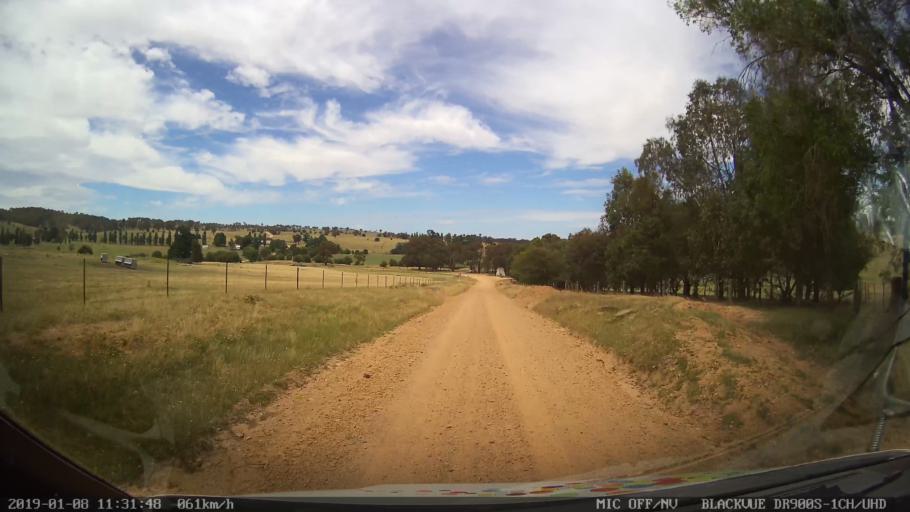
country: AU
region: New South Wales
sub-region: Guyra
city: Guyra
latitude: -30.3144
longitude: 151.5347
